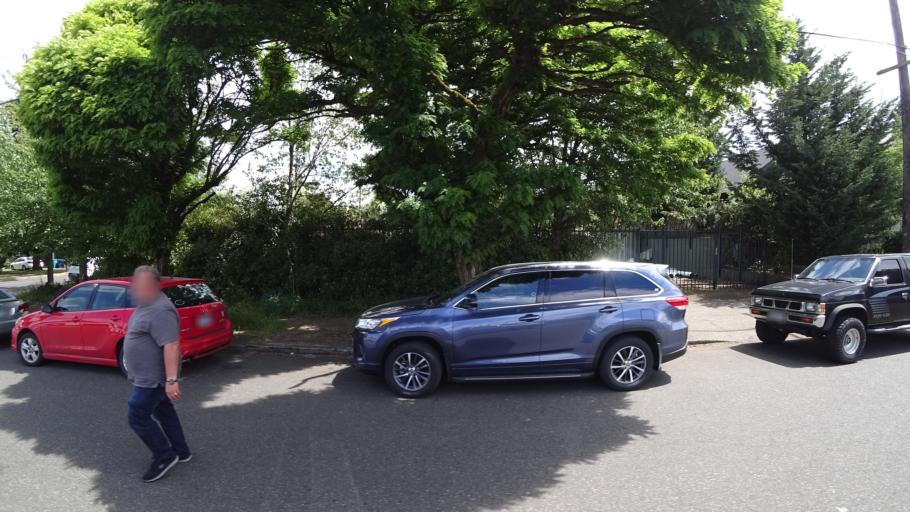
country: US
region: Oregon
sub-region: Washington County
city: West Haven
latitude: 45.5876
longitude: -122.7421
